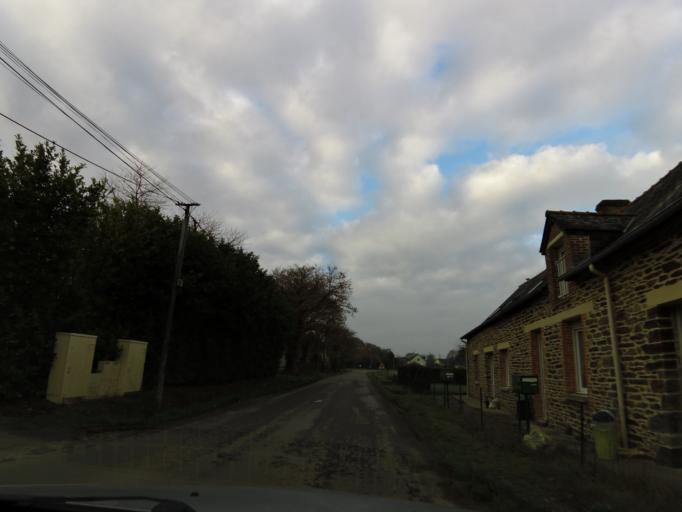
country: FR
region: Brittany
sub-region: Departement d'Ille-et-Vilaine
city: Chanteloup
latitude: 47.9690
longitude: -1.6422
